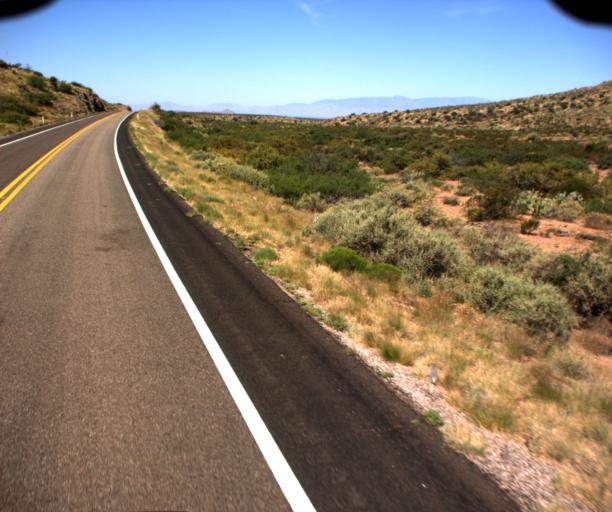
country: US
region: Arizona
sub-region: Greenlee County
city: Clifton
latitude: 32.7592
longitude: -109.3230
